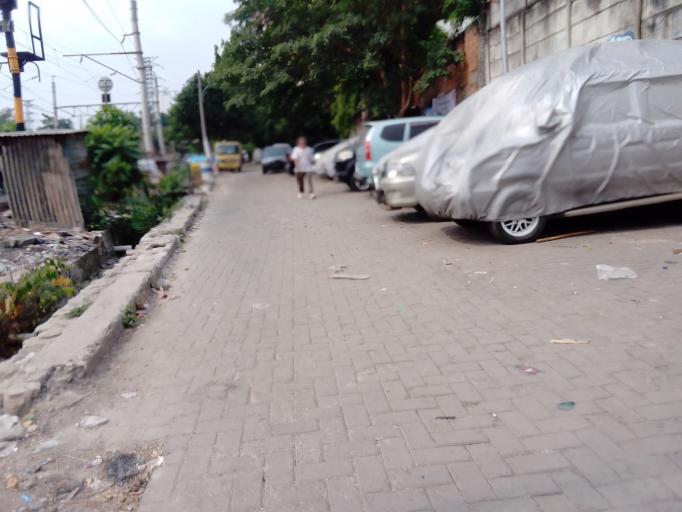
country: ID
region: Jakarta Raya
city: Jakarta
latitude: -6.2012
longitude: 106.8073
